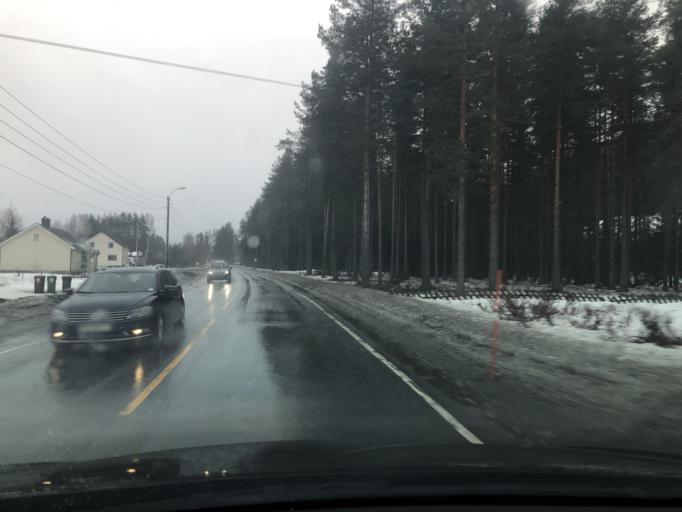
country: NO
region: Oppland
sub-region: Nordre Land
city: Dokka
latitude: 60.5703
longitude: 9.9811
